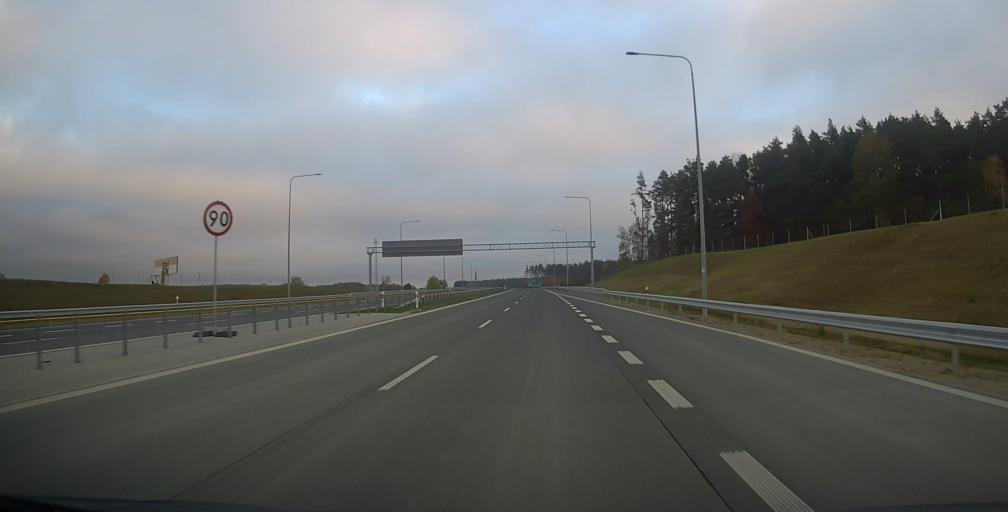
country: PL
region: Podlasie
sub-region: Powiat kolnenski
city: Stawiski
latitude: 53.4590
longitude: 22.1991
